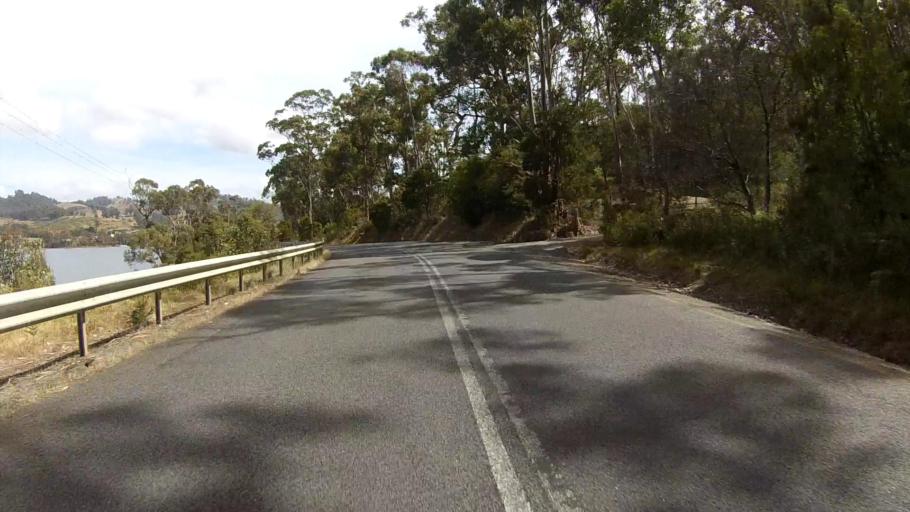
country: AU
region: Tasmania
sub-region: Huon Valley
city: Cygnet
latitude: -43.1825
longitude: 147.0959
